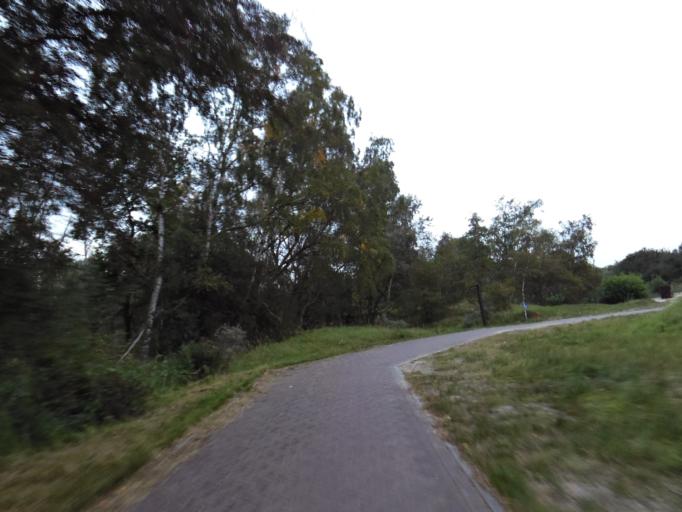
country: NL
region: South Holland
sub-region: Gemeente Leidschendam-Voorburg
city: Voorburg
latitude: 52.1151
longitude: 4.3355
